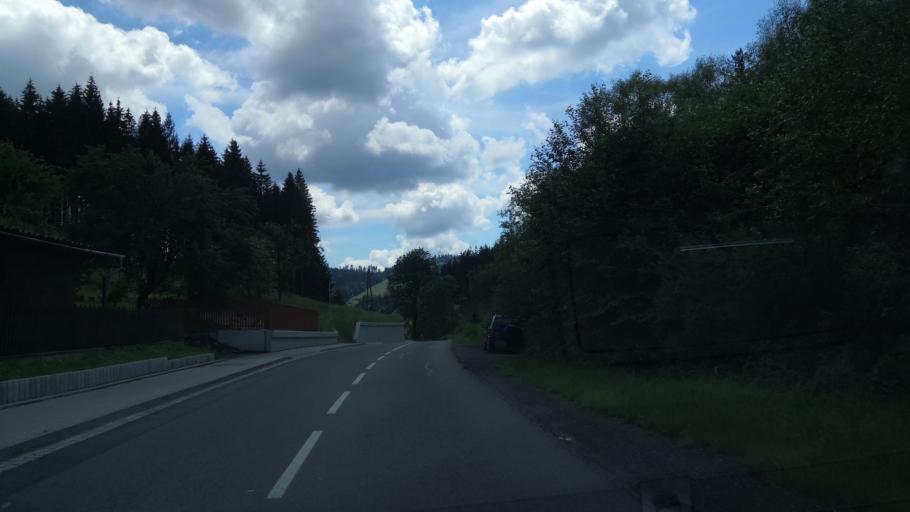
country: CZ
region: Zlin
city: Valasska Bystrice
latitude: 49.4217
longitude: 18.1173
